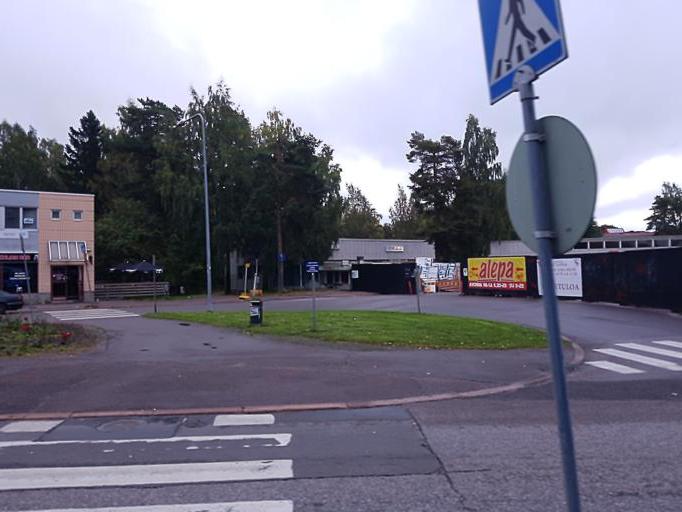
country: FI
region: Uusimaa
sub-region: Helsinki
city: Teekkarikylae
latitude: 60.2420
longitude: 24.8852
